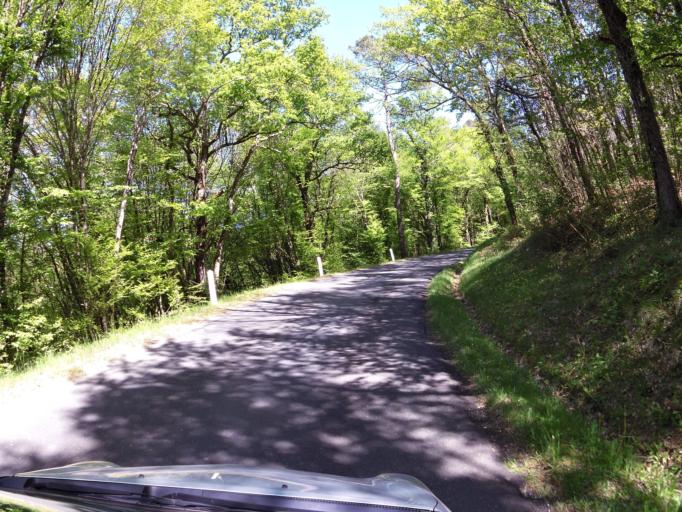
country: FR
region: Aquitaine
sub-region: Departement de la Dordogne
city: Sarlat-la-Caneda
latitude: 44.9231
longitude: 1.1537
